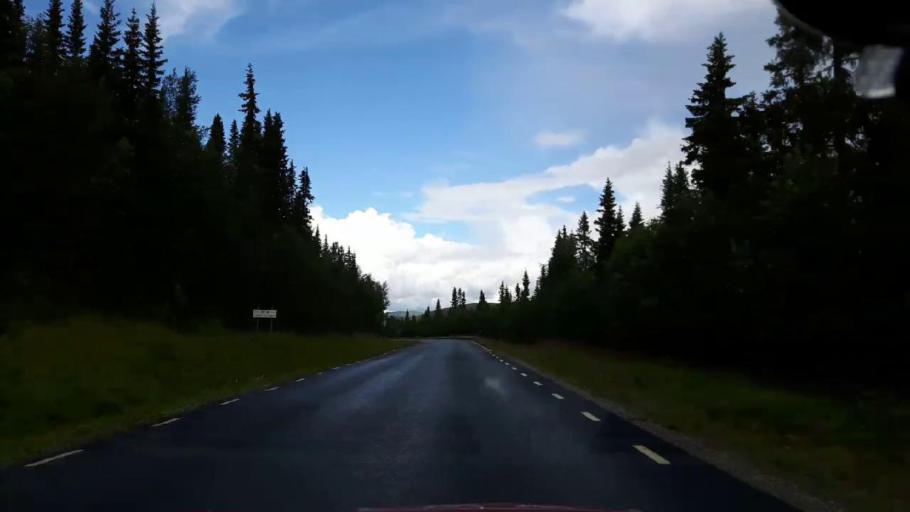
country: SE
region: Vaesterbotten
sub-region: Vilhelmina Kommun
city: Sjoberg
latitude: 64.9999
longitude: 15.1990
